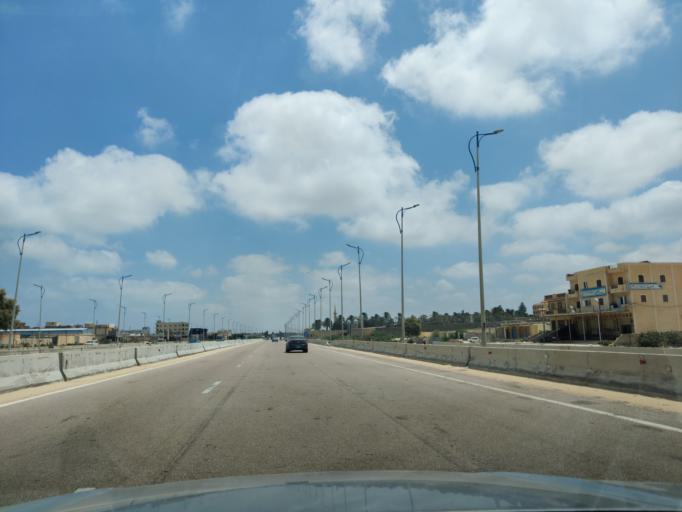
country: EG
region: Alexandria
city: Alexandria
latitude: 30.9827
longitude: 29.5813
